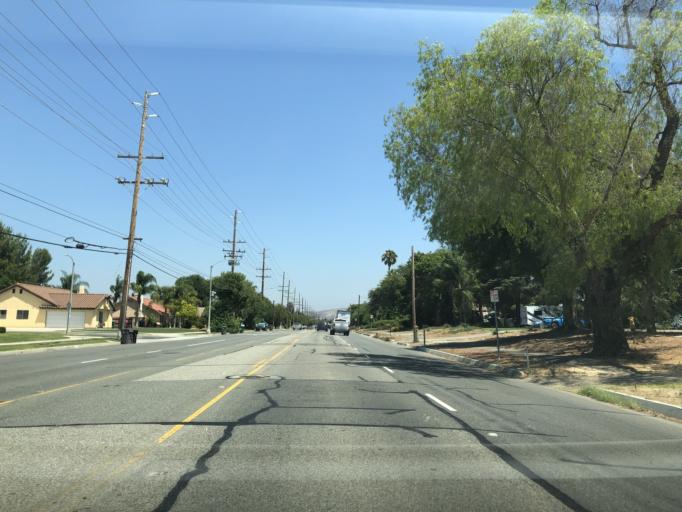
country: US
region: California
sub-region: Riverside County
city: Corona
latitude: 33.8581
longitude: -117.5852
